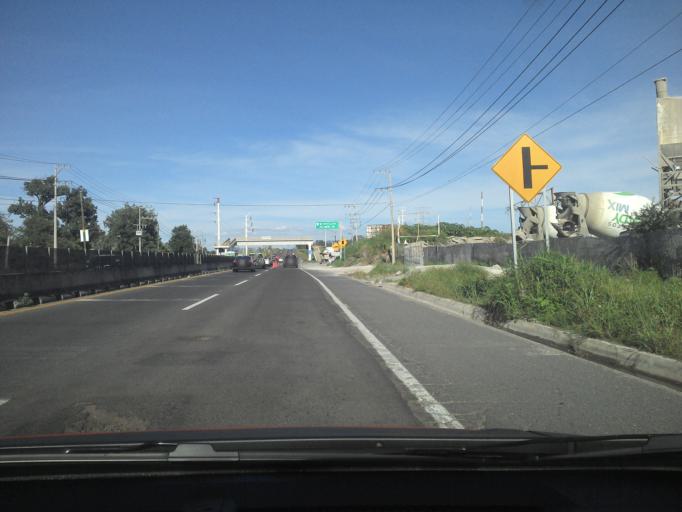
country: MX
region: Jalisco
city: Tala
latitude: 20.6691
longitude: -103.7155
